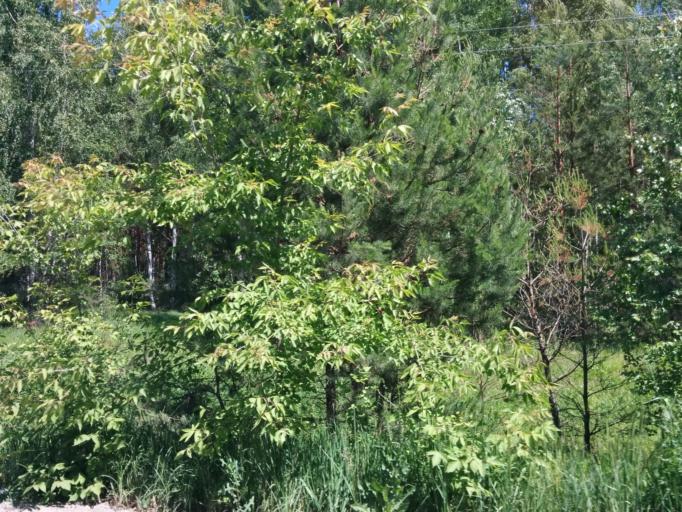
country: RU
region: Tambov
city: Morshansk
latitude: 53.6510
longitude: 41.8509
